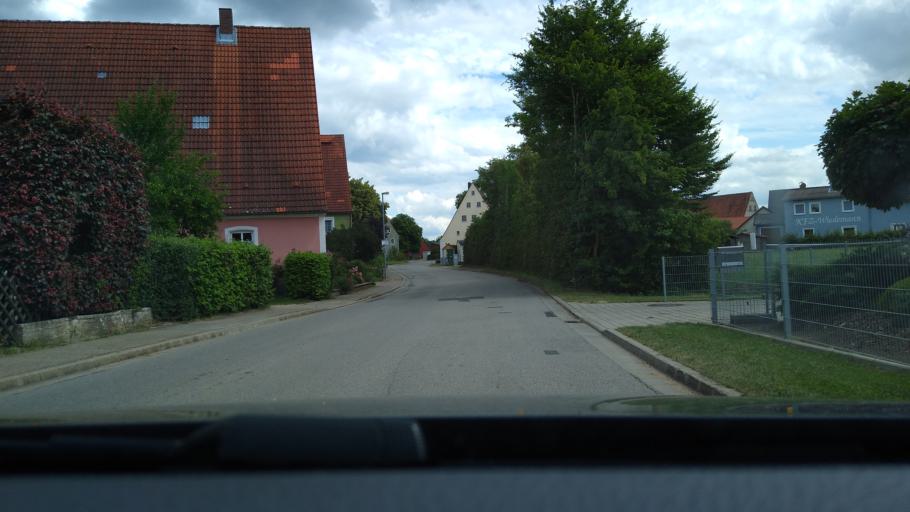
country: DE
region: Bavaria
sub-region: Regierungsbezirk Mittelfranken
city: Absberg
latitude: 49.1471
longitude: 10.8421
